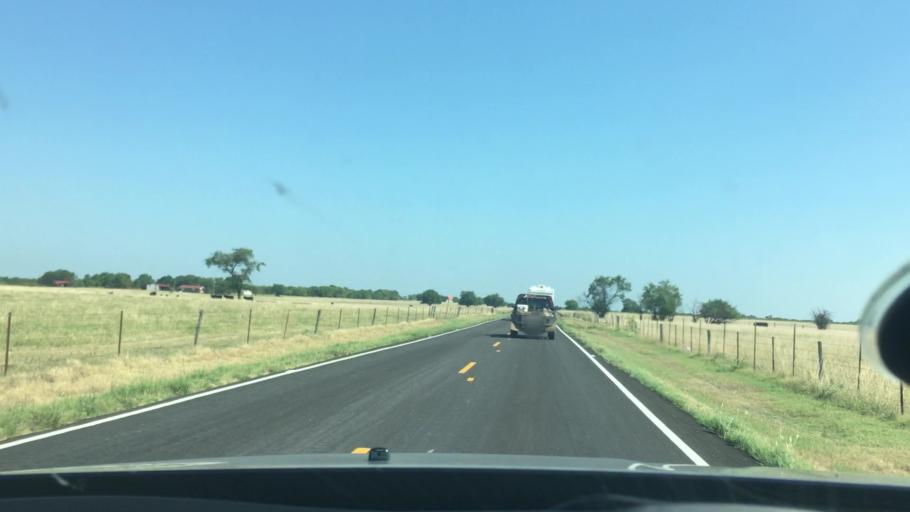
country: US
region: Oklahoma
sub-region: Johnston County
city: Tishomingo
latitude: 34.1744
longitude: -96.5106
